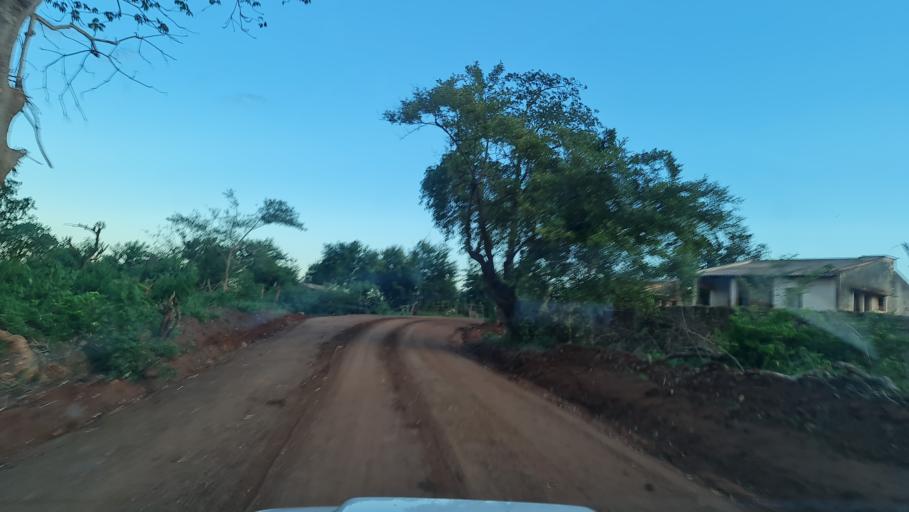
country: MZ
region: Nampula
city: Ilha de Mocambique
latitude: -14.9819
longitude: 40.0942
